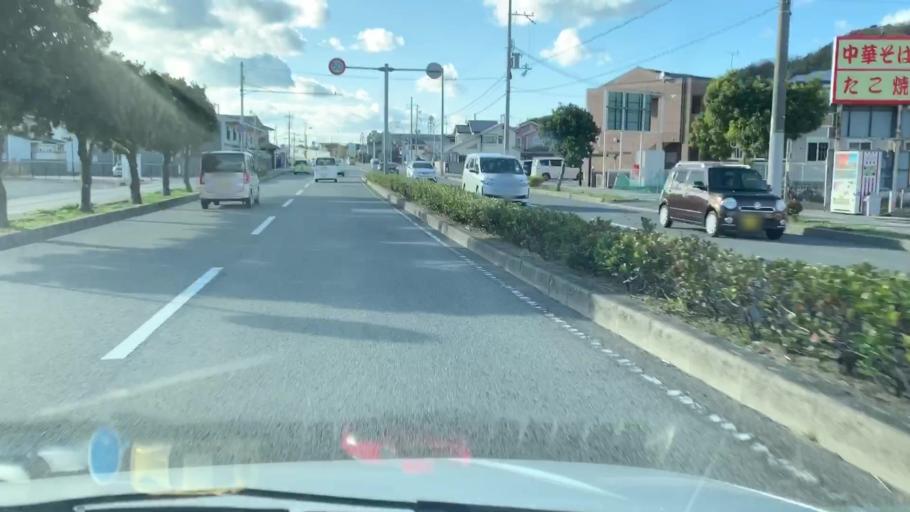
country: JP
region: Wakayama
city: Wakayama-shi
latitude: 34.2594
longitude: 135.1624
